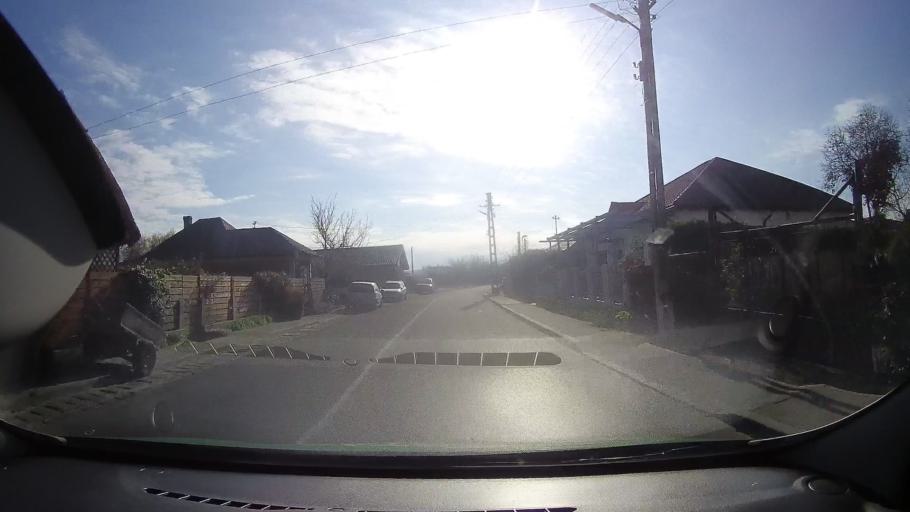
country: RO
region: Tulcea
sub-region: Comuna Murighiol
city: Murighiol
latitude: 45.0378
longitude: 29.1662
